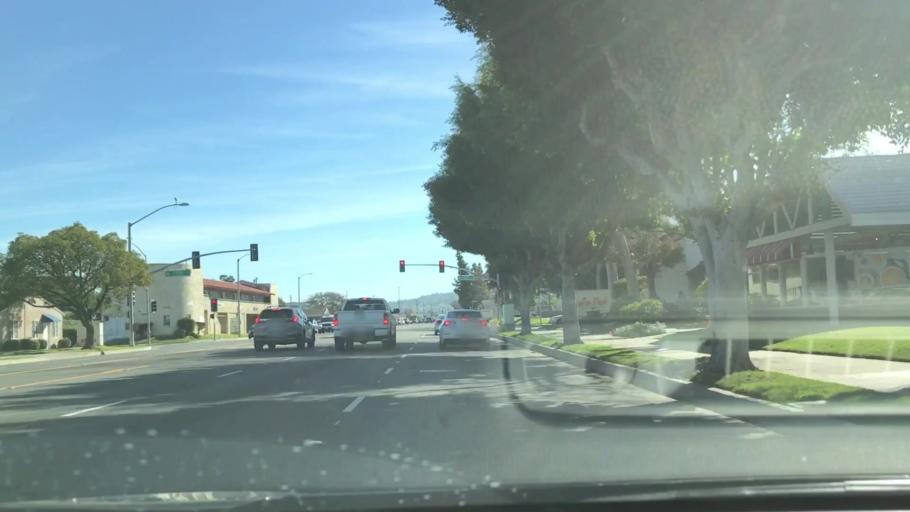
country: US
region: California
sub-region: Los Angeles County
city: Lomita
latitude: 33.8106
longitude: -118.3282
